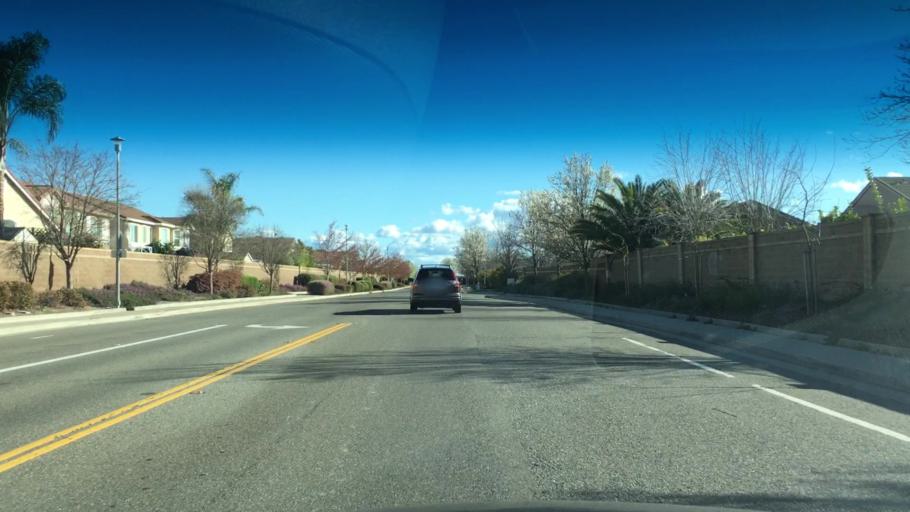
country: US
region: California
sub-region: Sacramento County
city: Laguna
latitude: 38.4476
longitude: -121.3995
